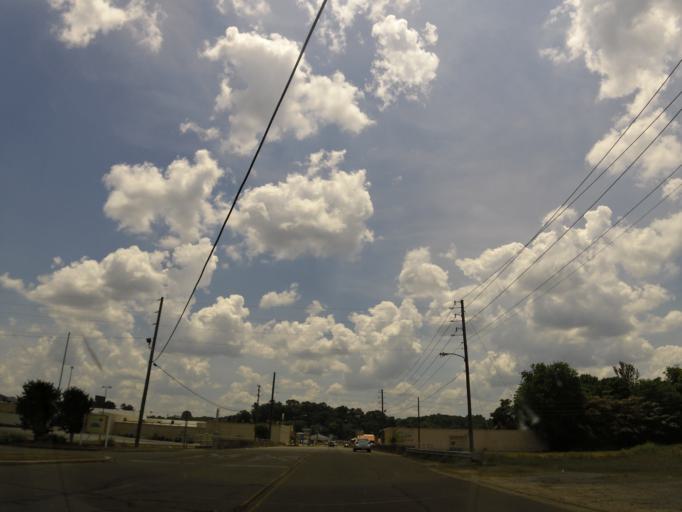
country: US
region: Mississippi
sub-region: Lauderdale County
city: Meridian
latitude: 32.3589
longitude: -88.6900
